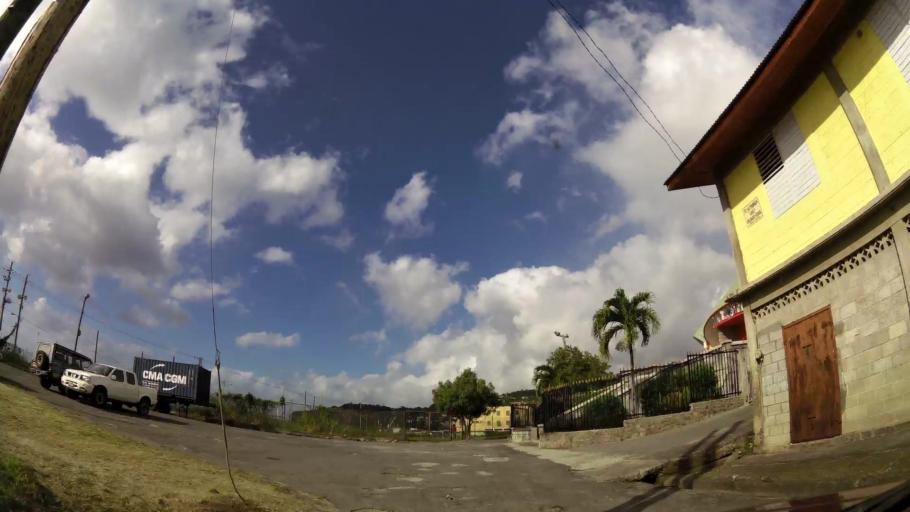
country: DM
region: Saint George
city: Roseau
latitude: 15.3046
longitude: -61.3894
